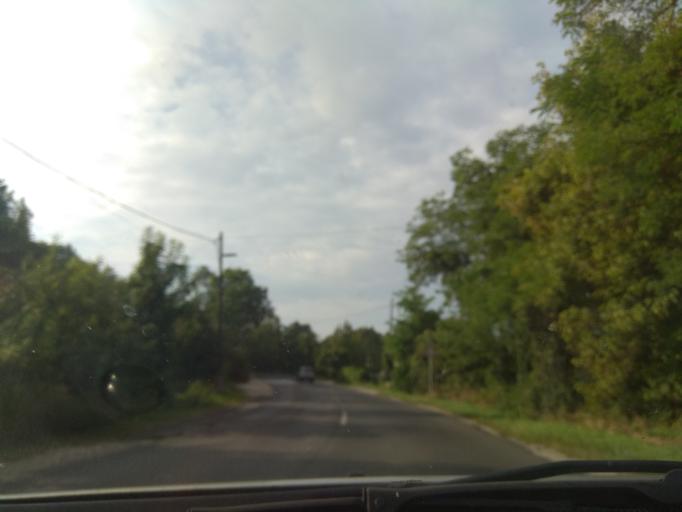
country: HU
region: Borsod-Abauj-Zemplen
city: Miskolc
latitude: 48.0879
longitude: 20.7522
